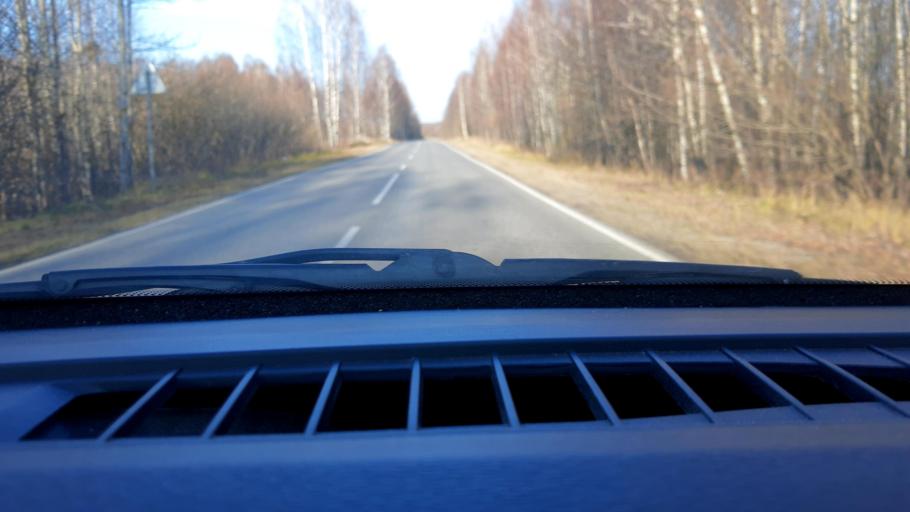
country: RU
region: Nizjnij Novgorod
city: Neklyudovo
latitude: 56.5073
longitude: 43.8427
